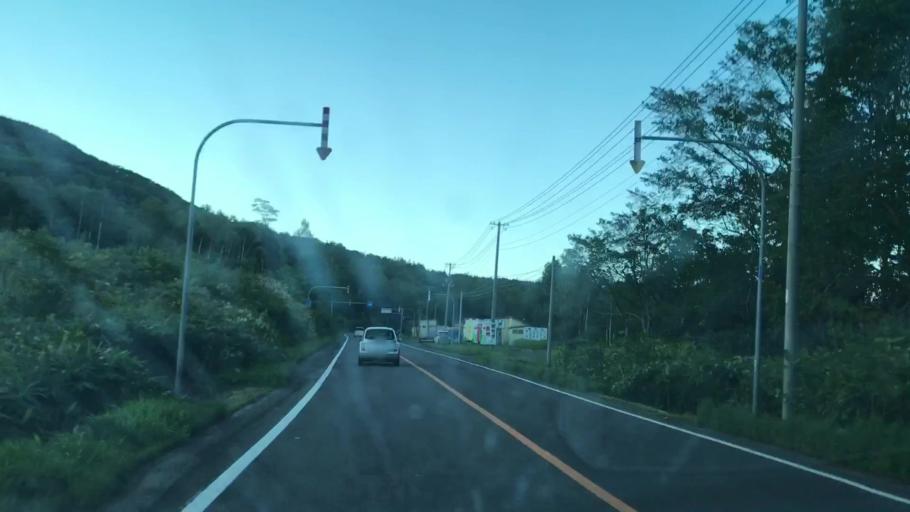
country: JP
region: Hokkaido
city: Niseko Town
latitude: 42.7634
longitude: 140.9292
